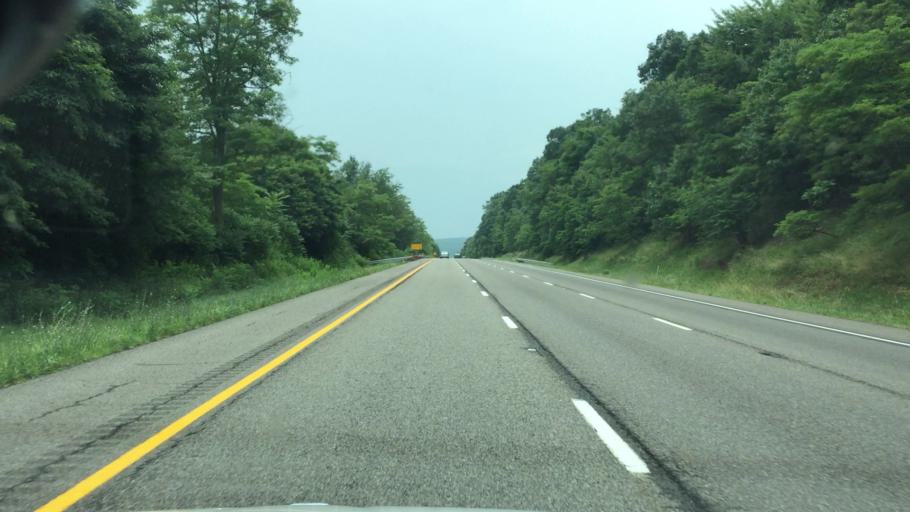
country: US
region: West Virginia
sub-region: Morgan County
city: Berkeley Springs
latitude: 39.6773
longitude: -78.4097
